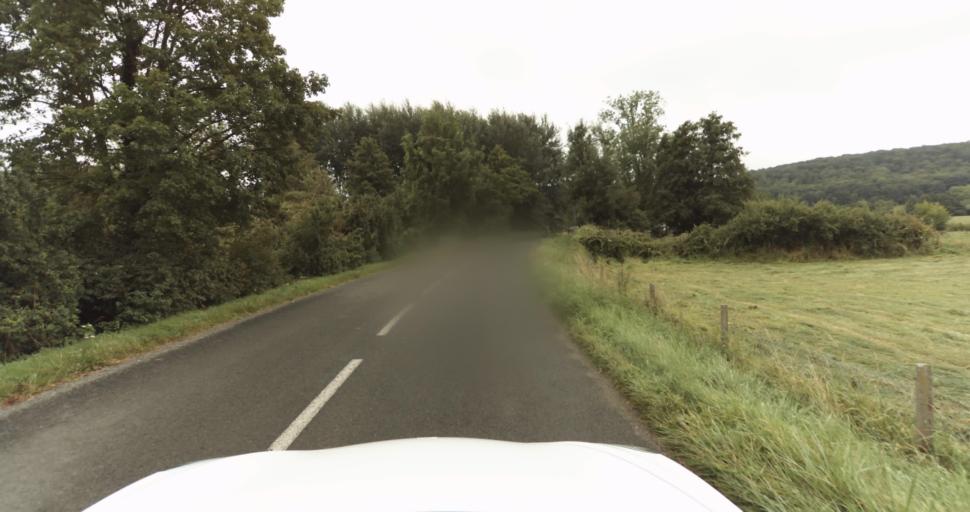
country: FR
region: Haute-Normandie
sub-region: Departement de l'Eure
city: Aviron
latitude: 49.0994
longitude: 1.1138
